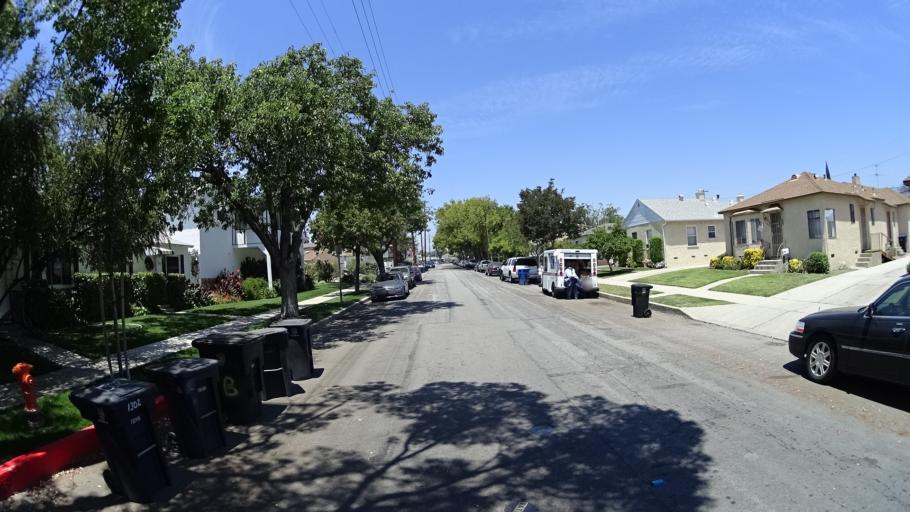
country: US
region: California
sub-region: Los Angeles County
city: North Hollywood
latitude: 34.1734
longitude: -118.3485
